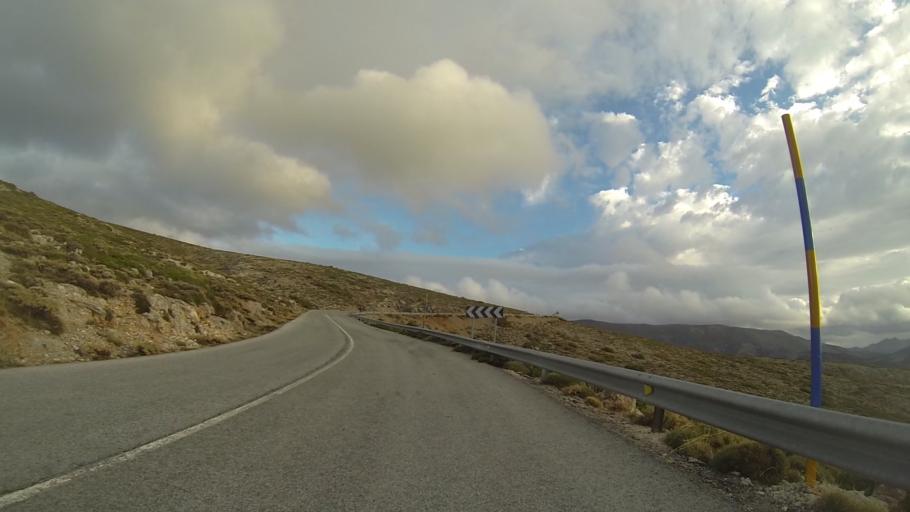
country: ES
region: Andalusia
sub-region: Provincia de Granada
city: Guejar-Sierra
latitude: 37.1201
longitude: -3.4316
